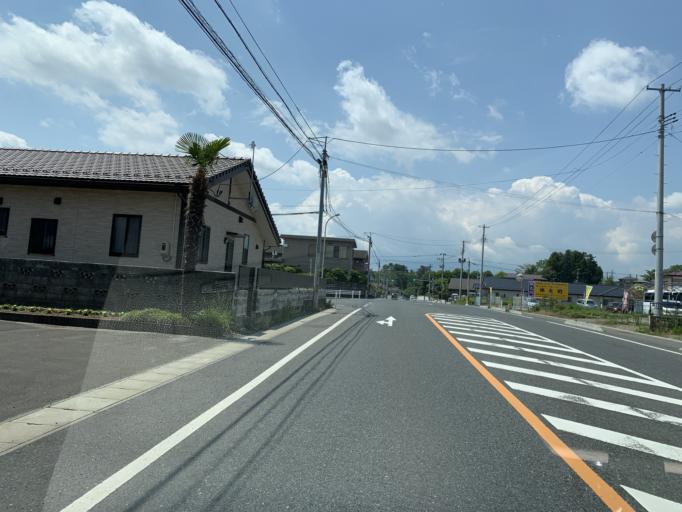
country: JP
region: Miyagi
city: Kogota
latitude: 38.5420
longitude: 141.0589
